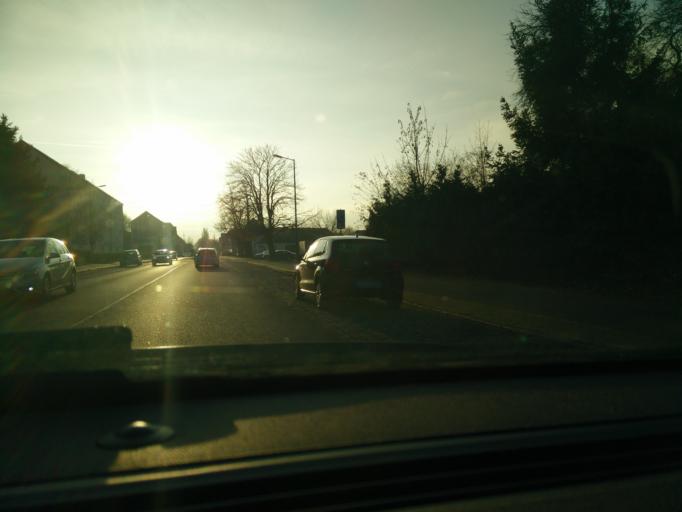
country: DE
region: Saxony
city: Taucha
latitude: 51.3394
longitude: 12.4765
